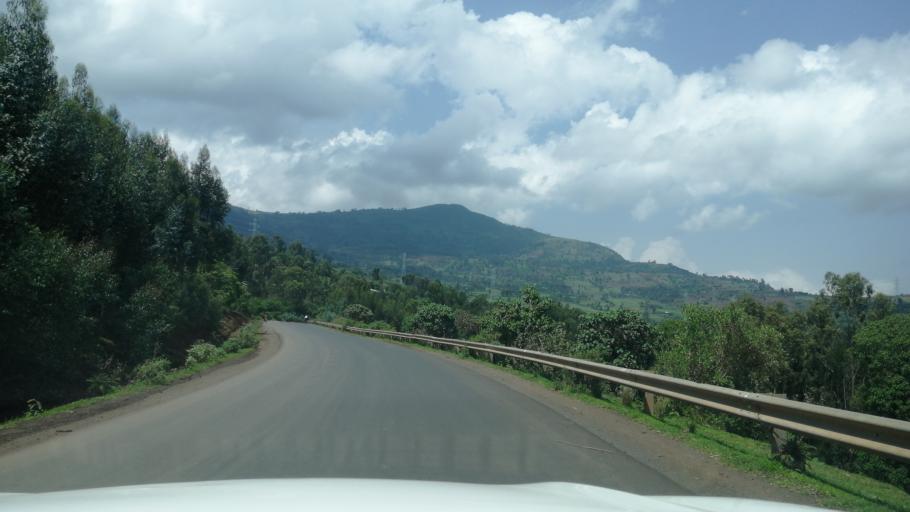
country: ET
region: Oromiya
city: Gedo
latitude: 8.9747
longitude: 37.5850
